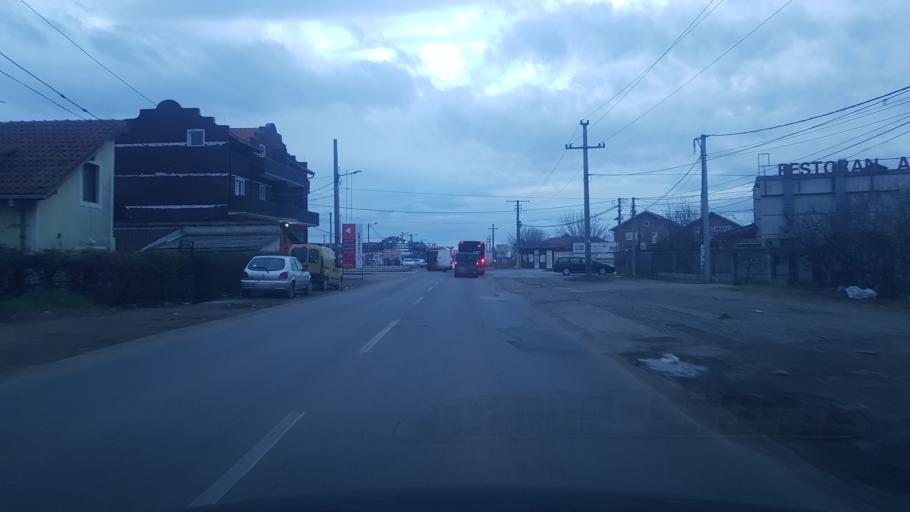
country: RS
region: Central Serbia
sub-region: Belgrade
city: Surcin
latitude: 44.8038
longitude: 20.3439
